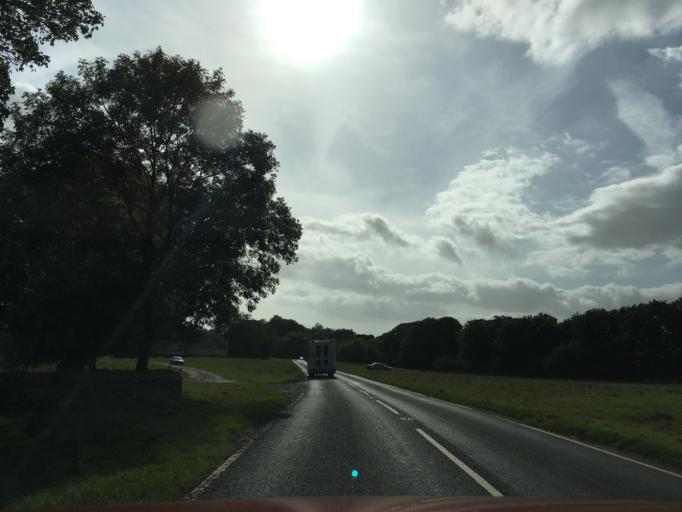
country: GB
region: England
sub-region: Gloucestershire
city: Nailsworth
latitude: 51.7215
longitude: -2.2515
